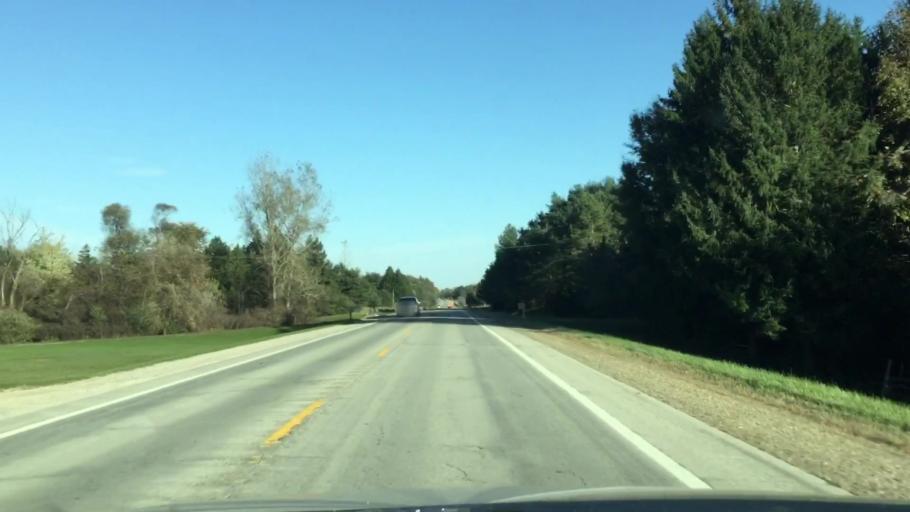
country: US
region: Michigan
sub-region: Lapeer County
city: North Branch
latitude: 43.2283
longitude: -83.2498
